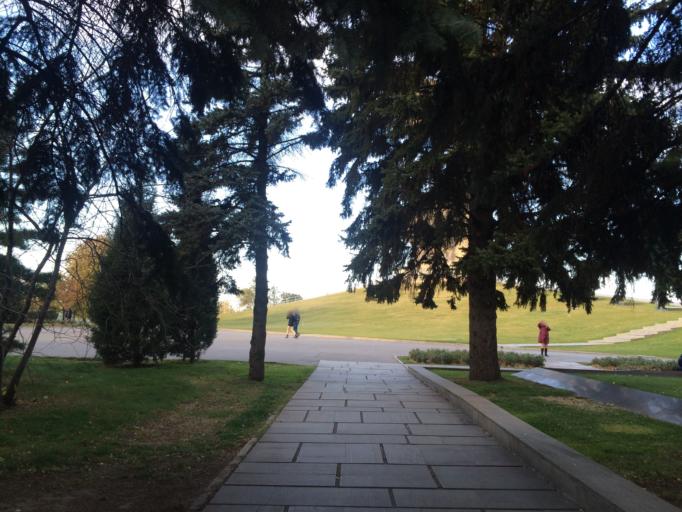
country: RU
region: Volgograd
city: Volgograd
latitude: 48.7411
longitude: 44.5367
